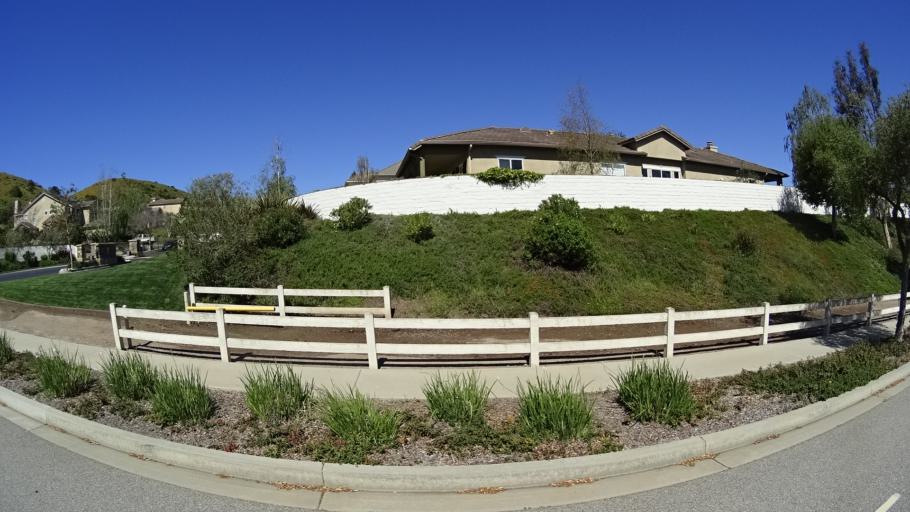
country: US
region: California
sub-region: Ventura County
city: Casa Conejo
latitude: 34.1707
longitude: -118.9905
